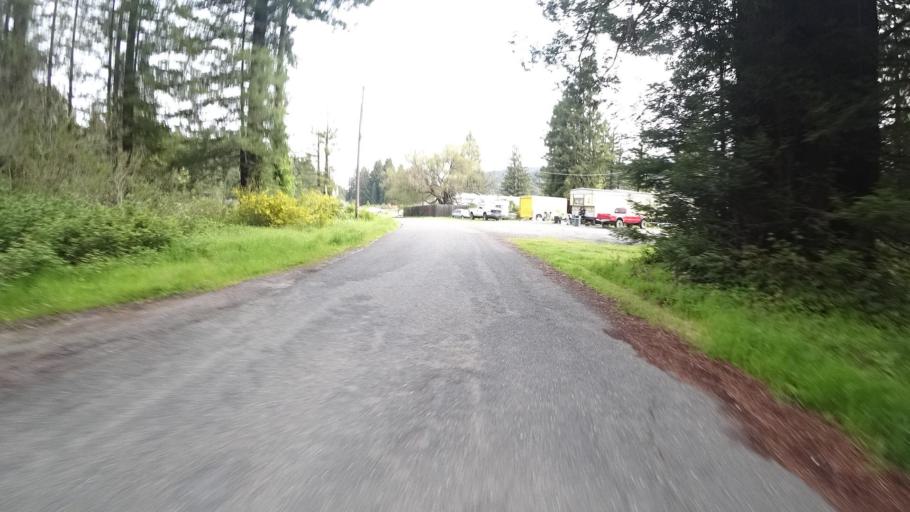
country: US
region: California
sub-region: Humboldt County
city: Redway
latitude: 40.3436
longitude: -123.9165
